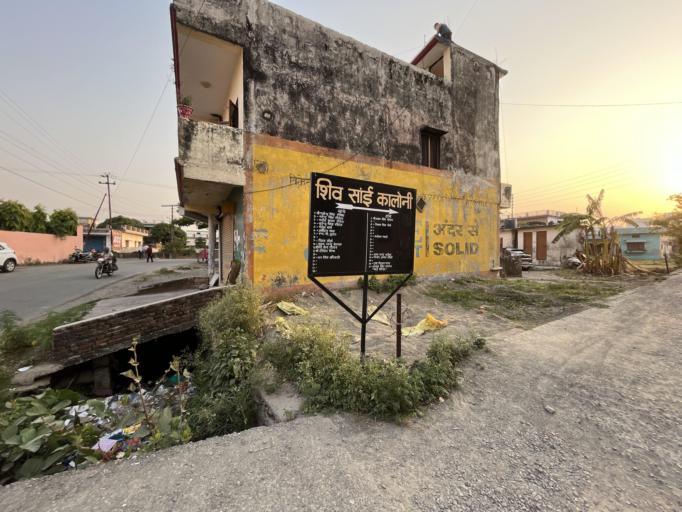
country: IN
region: Uttarakhand
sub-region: Naini Tal
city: Haldwani
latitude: 29.2279
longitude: 79.5095
